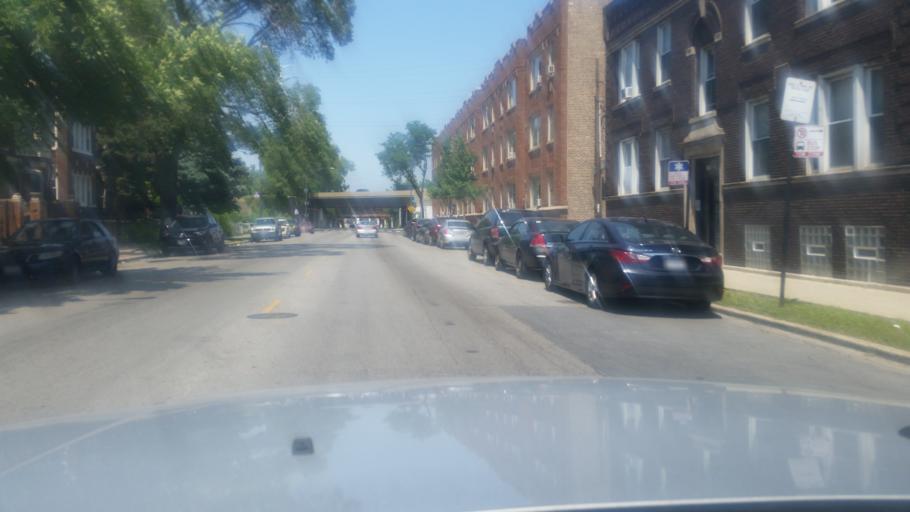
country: US
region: Illinois
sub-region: Cook County
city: Chicago
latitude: 41.7696
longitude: -87.6153
